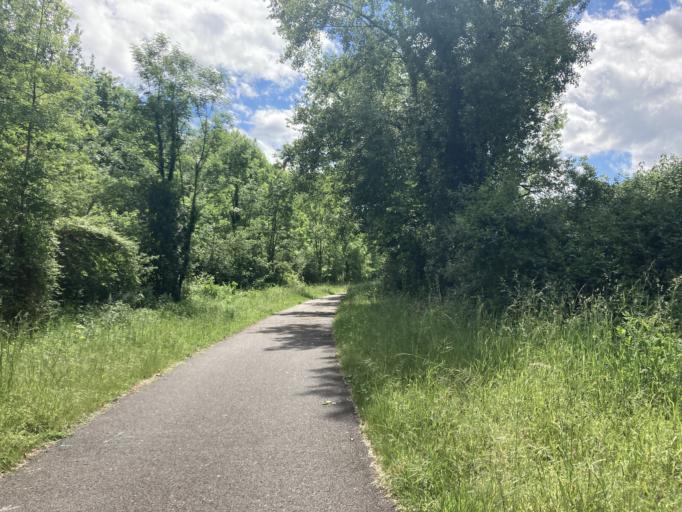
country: FR
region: Aquitaine
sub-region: Departement des Pyrenees-Atlantiques
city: Artiguelouve
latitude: 43.3269
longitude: -0.4602
